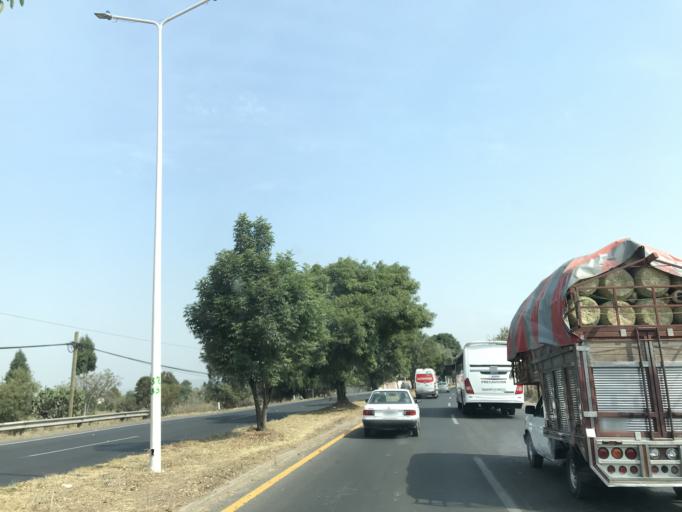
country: MX
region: Tlaxcala
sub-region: Teolocholco
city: Teolocholco
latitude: 19.2563
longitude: -98.2000
